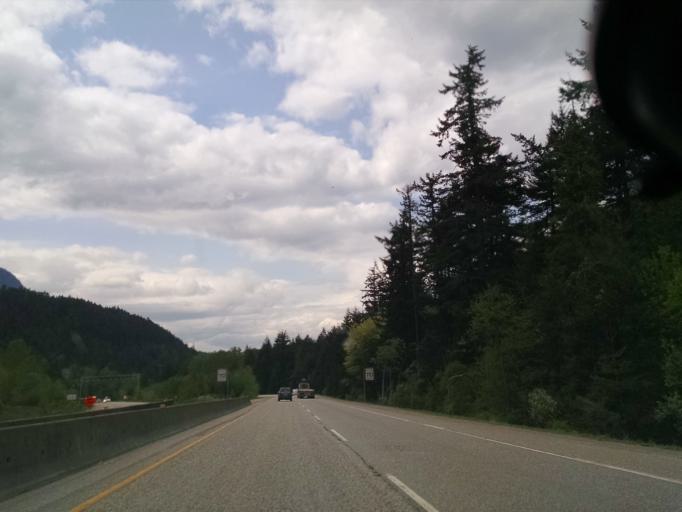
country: CA
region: British Columbia
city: Hope
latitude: 49.3791
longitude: -121.3352
